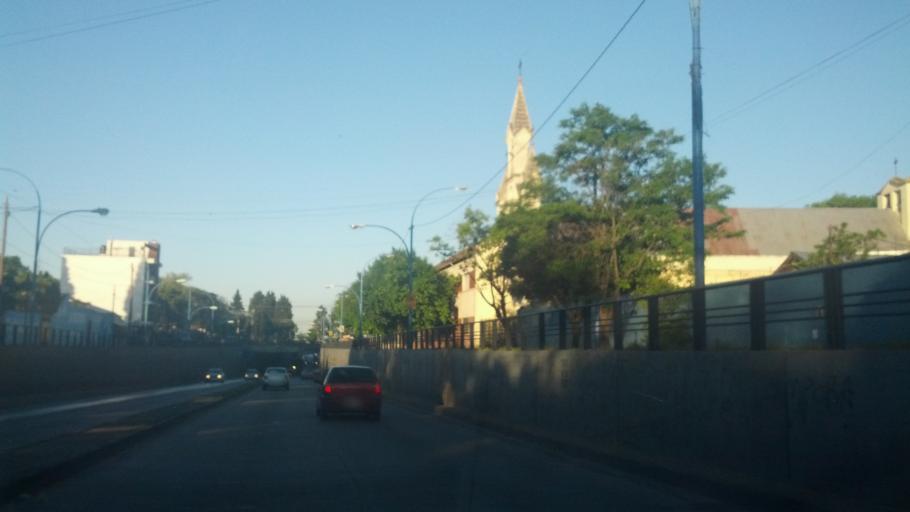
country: AR
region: Buenos Aires
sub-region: Partido de Lomas de Zamora
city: Lomas de Zamora
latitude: -34.7807
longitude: -58.3982
